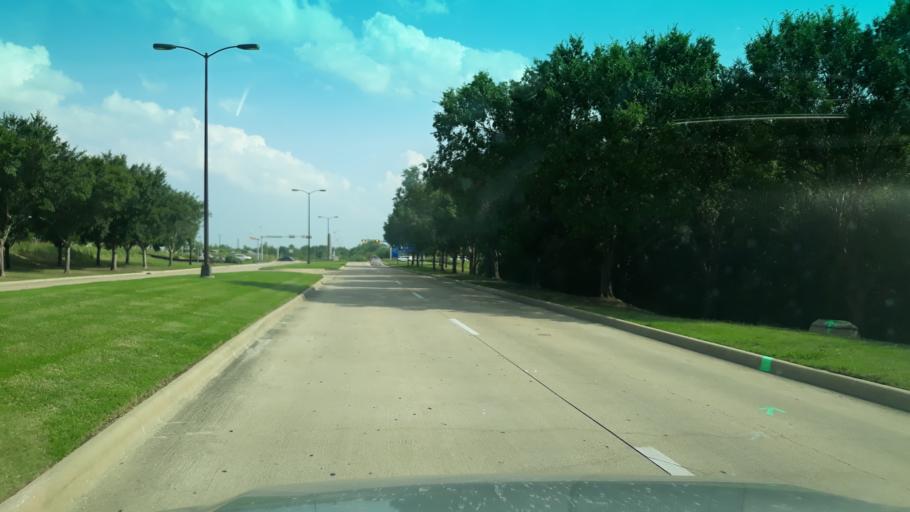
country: US
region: Texas
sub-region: Tarrant County
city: Euless
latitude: 32.8546
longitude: -97.0326
